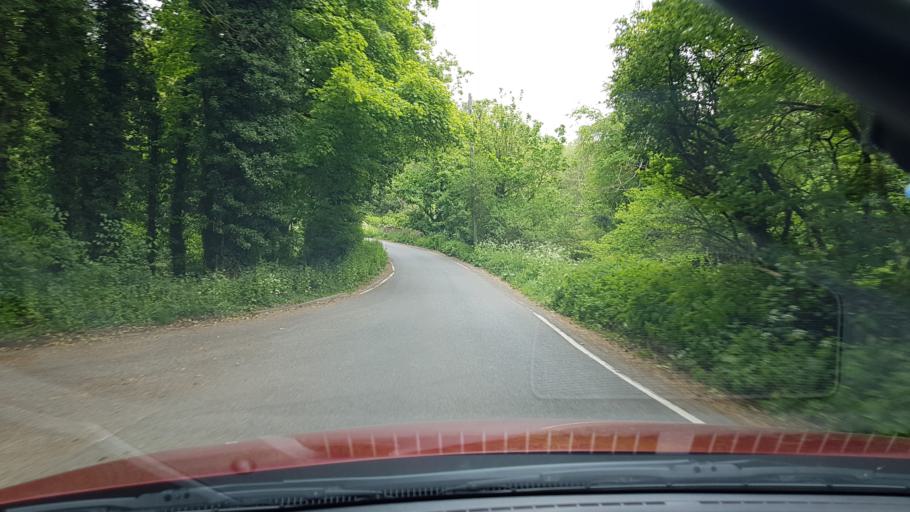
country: GB
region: England
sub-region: Rotherham
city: Maltby
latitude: 53.4059
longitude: -1.1912
